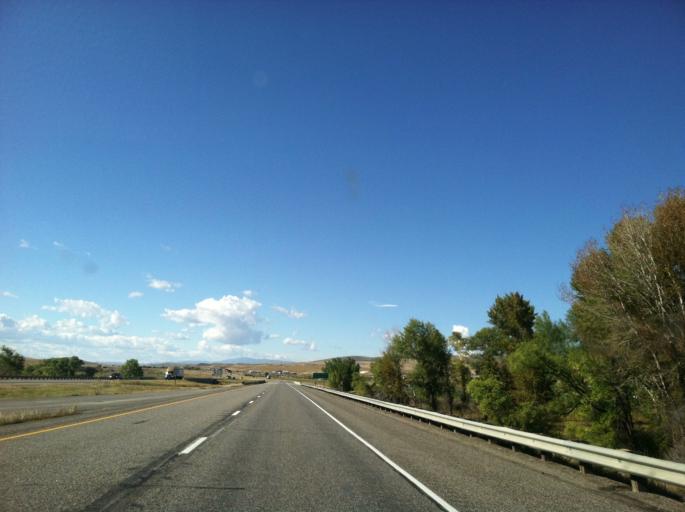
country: US
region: Montana
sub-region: Gallatin County
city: Three Forks
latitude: 45.9088
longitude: -111.5462
